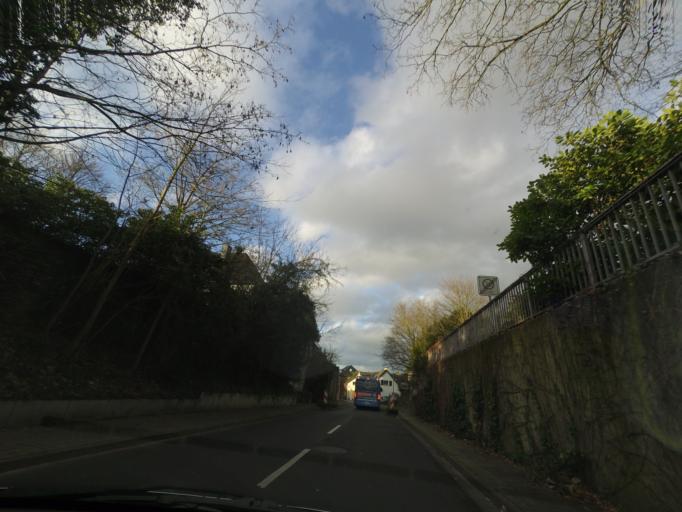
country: DE
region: North Rhine-Westphalia
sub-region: Regierungsbezirk Dusseldorf
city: Grevenbroich
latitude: 51.1170
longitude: 6.5645
